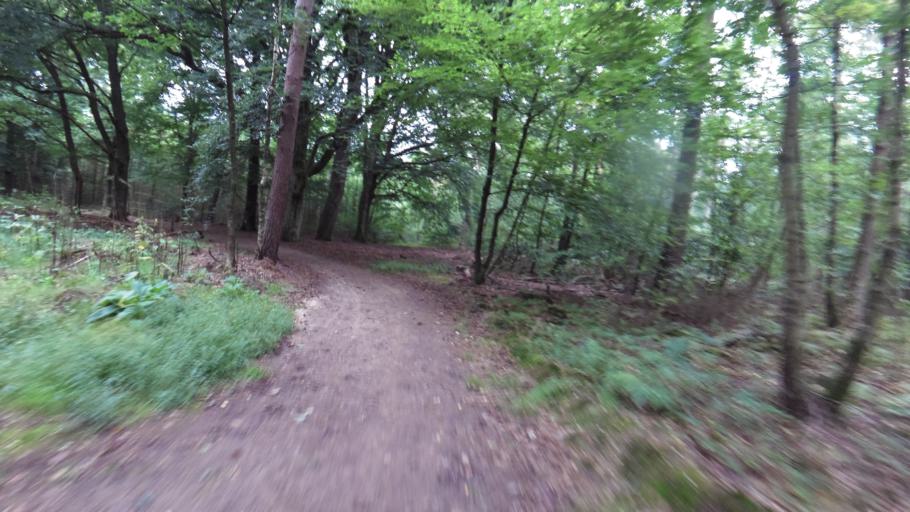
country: NL
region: Gelderland
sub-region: Gemeente Renkum
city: Renkum
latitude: 51.9940
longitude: 5.7234
